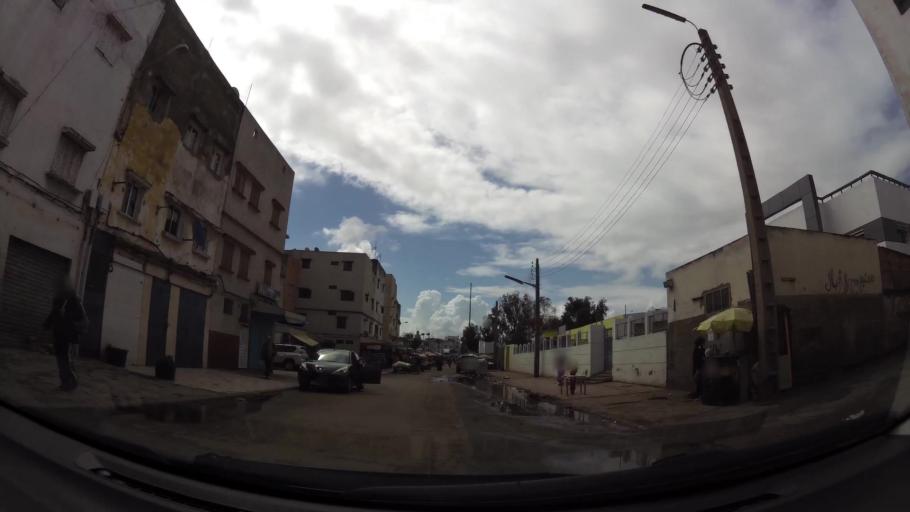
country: MA
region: Grand Casablanca
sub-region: Casablanca
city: Casablanca
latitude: 33.5731
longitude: -7.6792
